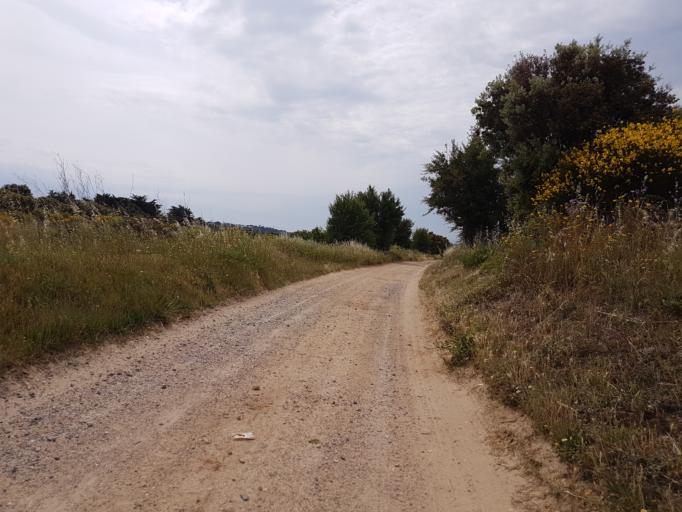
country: FR
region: Languedoc-Roussillon
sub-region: Departement de l'Herault
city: Portiragnes
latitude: 43.3110
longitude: 3.3751
